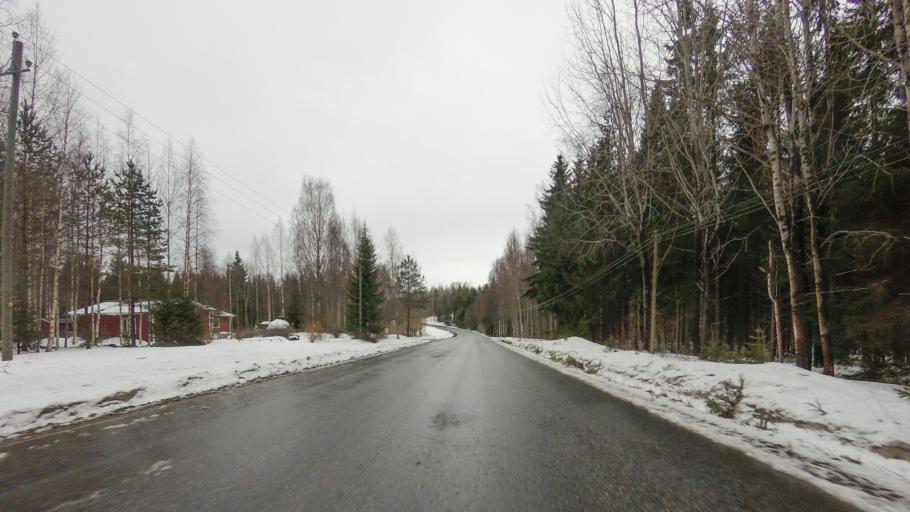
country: FI
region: Southern Savonia
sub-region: Savonlinna
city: Savonlinna
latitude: 61.9349
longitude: 28.8726
